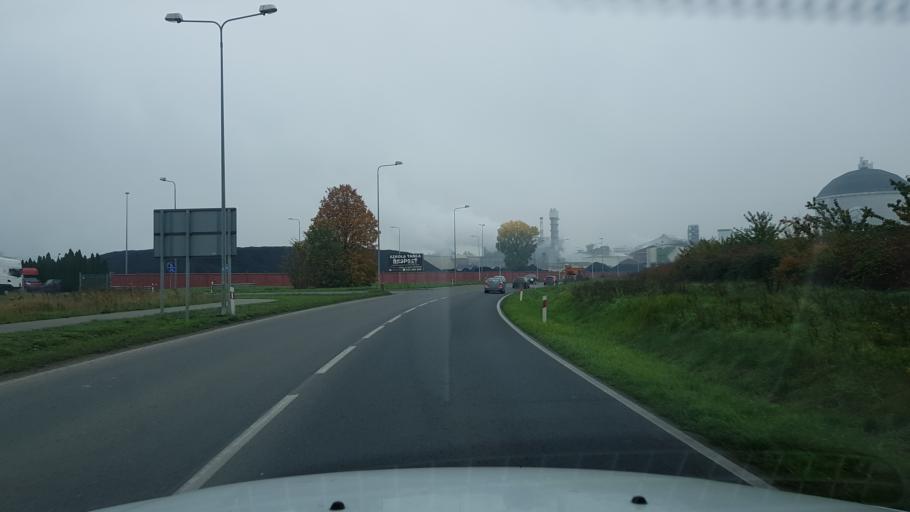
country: PL
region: West Pomeranian Voivodeship
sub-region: Powiat stargardzki
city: Stargard Szczecinski
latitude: 53.3033
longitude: 15.0217
